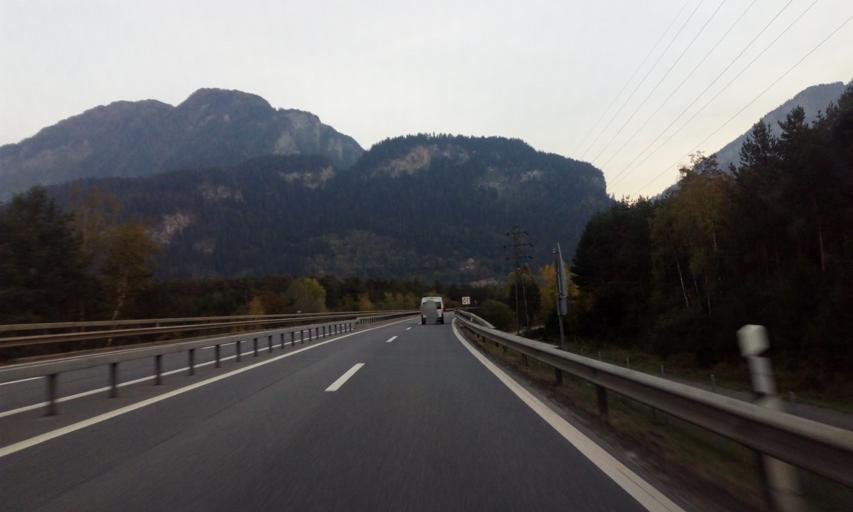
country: CH
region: Grisons
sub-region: Hinterrhein District
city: Thusis
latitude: 46.7100
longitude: 9.4483
